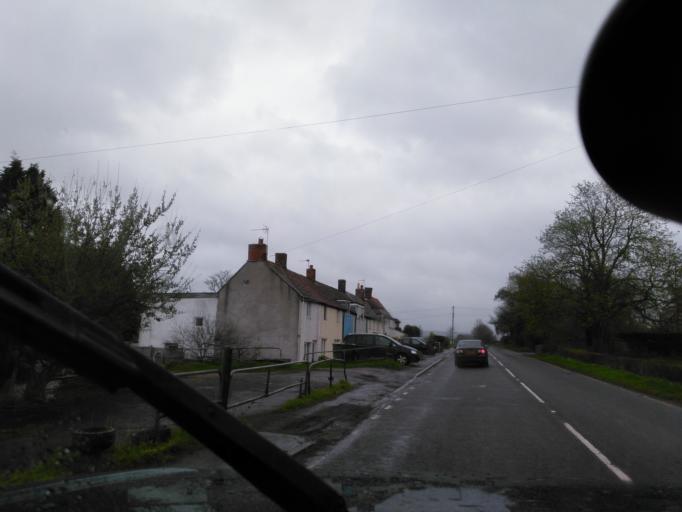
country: GB
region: England
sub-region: Somerset
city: Wells
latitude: 51.1515
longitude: -2.6280
